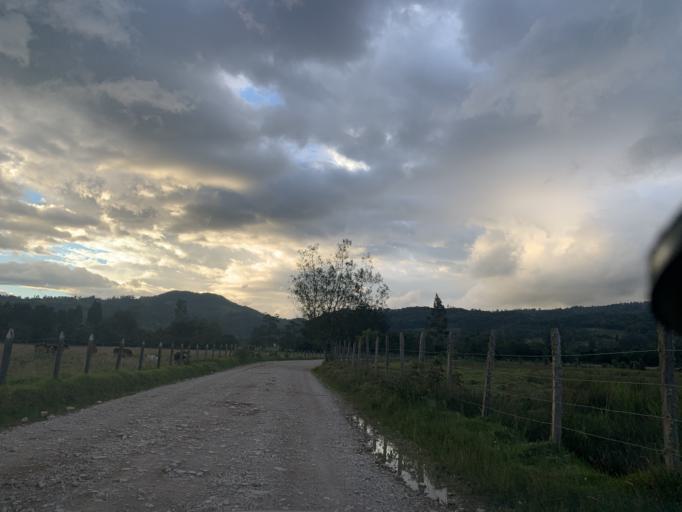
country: CO
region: Boyaca
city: La Capilla
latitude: 5.7344
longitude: -73.4980
